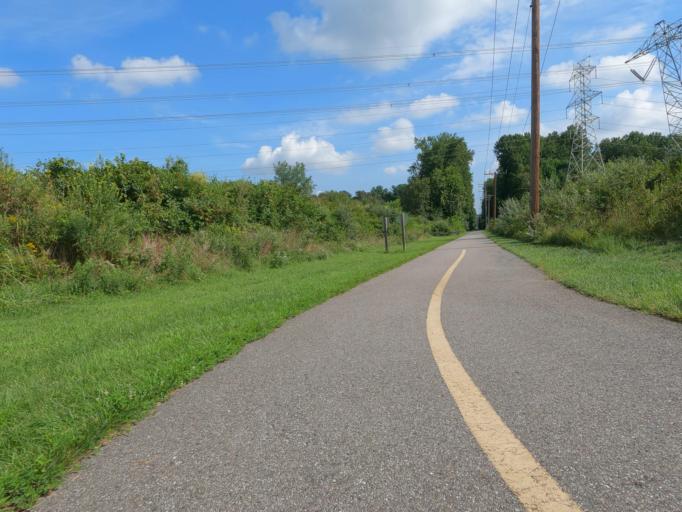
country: US
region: Maryland
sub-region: Anne Arundel County
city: Crofton
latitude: 39.0303
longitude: -76.7250
